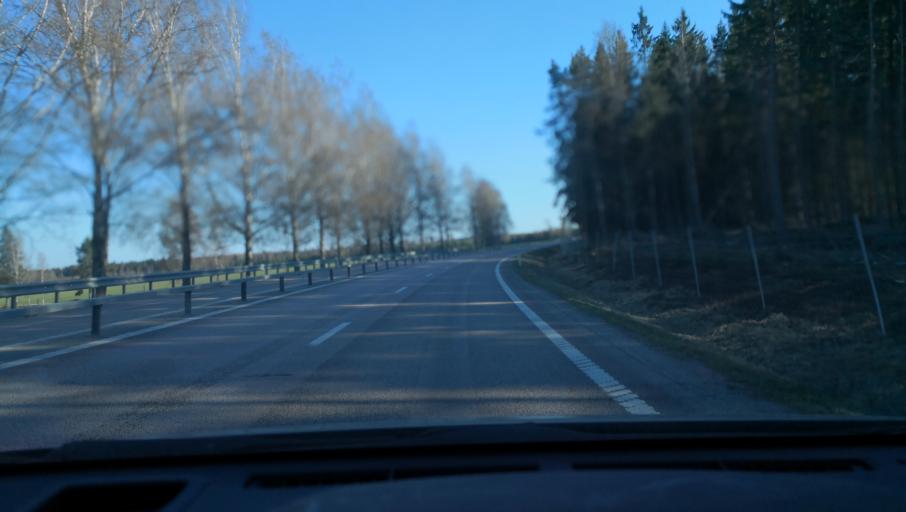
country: SE
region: Vaestmanland
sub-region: Vasteras
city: Tillberga
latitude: 59.7969
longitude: 16.5637
